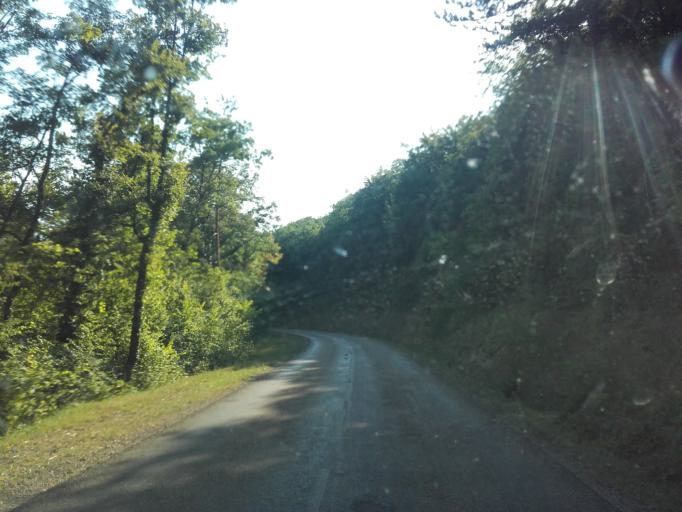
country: FR
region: Bourgogne
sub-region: Departement de l'Yonne
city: Chablis
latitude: 47.8409
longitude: 3.8368
